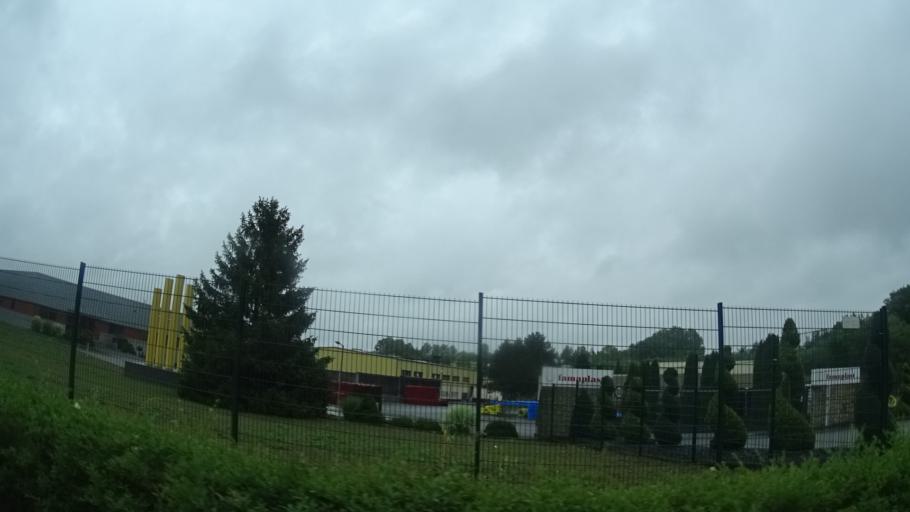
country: LU
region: Luxembourg
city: Soleuvre
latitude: 49.5348
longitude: 5.9404
